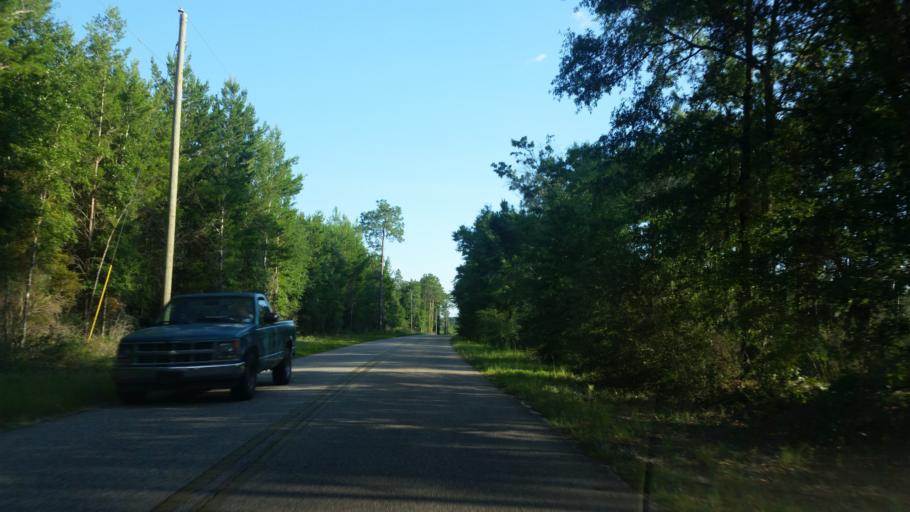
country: US
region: Florida
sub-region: Santa Rosa County
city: East Milton
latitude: 30.6741
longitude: -86.8767
